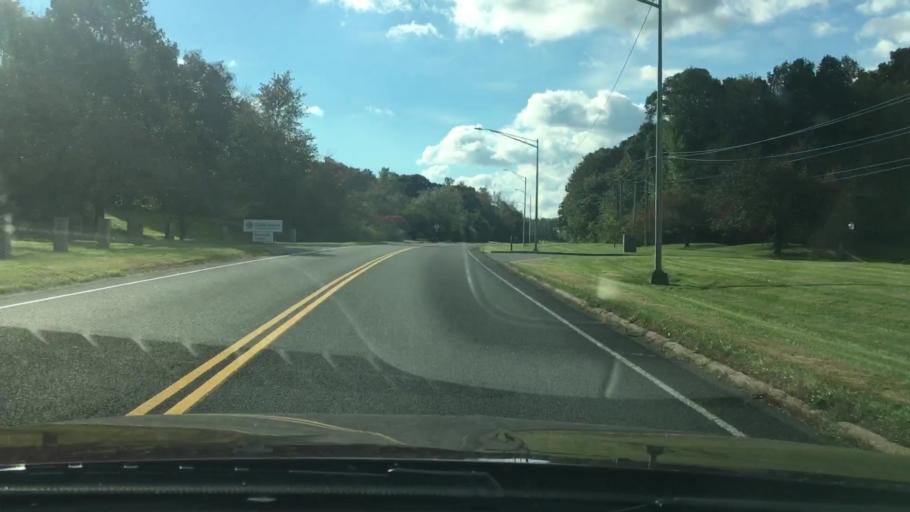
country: US
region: Connecticut
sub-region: New Haven County
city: Meriden
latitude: 41.5017
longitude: -72.7644
